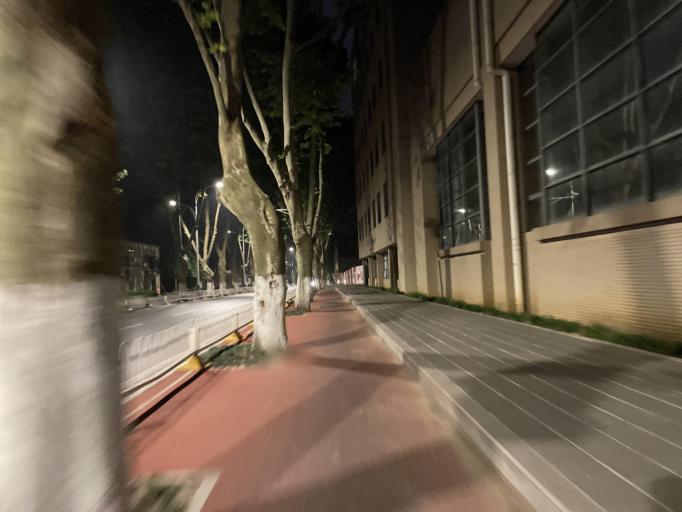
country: CN
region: Hubei
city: Guanshan
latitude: 30.5182
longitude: 114.4098
